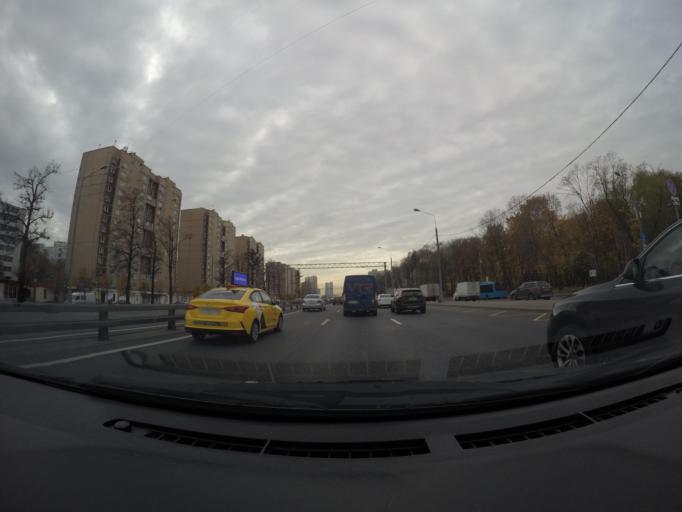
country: RU
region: Moscow
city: Vatutino
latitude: 55.8576
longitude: 37.6858
